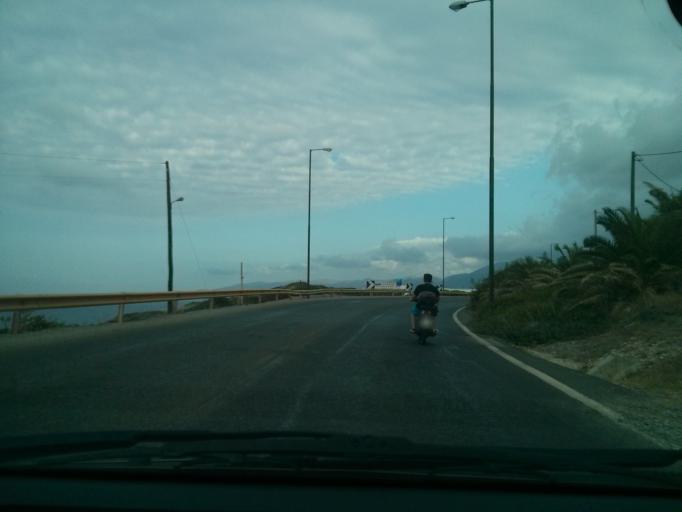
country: GR
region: Crete
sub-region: Nomos Irakleiou
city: Stalis
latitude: 35.3045
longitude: 25.4162
